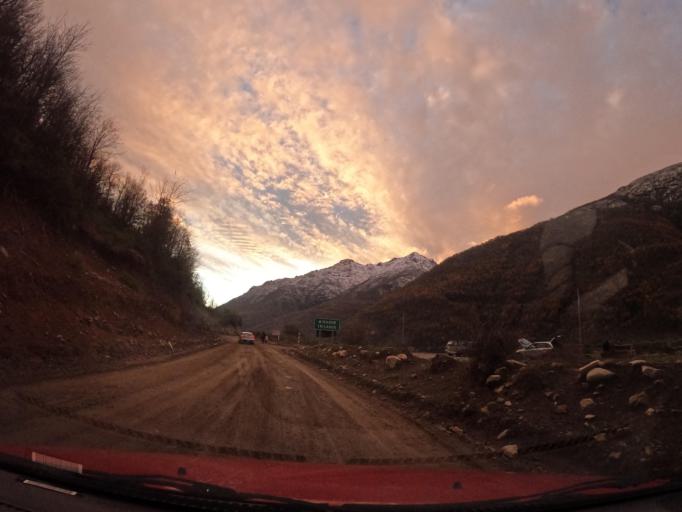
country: CL
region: Maule
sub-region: Provincia de Linares
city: Colbun
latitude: -35.8562
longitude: -71.1733
